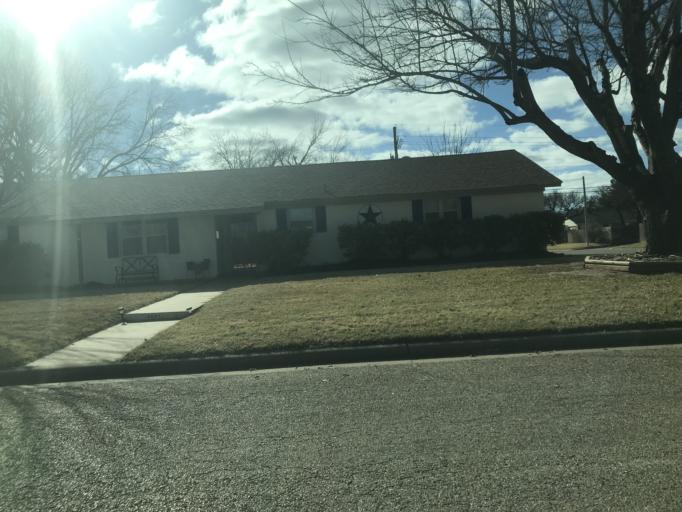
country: US
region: Texas
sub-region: Taylor County
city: Abilene
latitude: 32.4637
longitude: -99.7728
